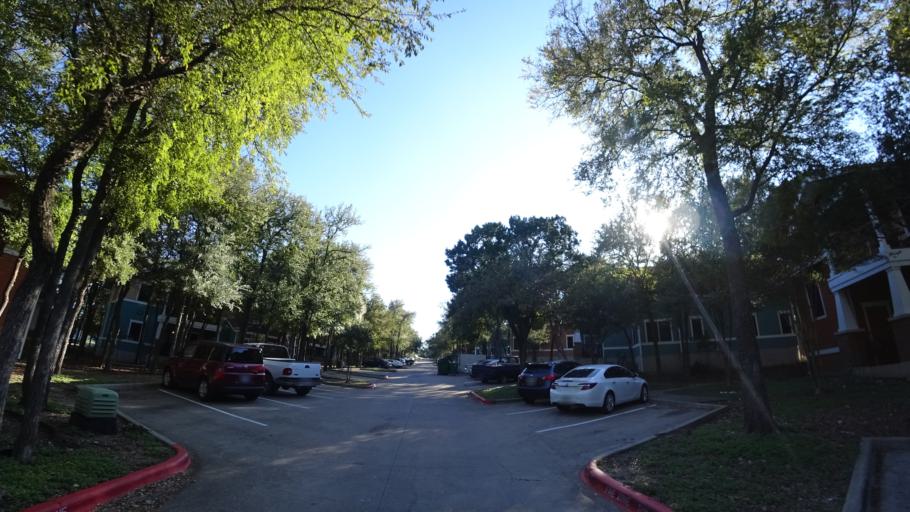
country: US
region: Texas
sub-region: Travis County
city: Austin
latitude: 30.2233
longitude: -97.7312
